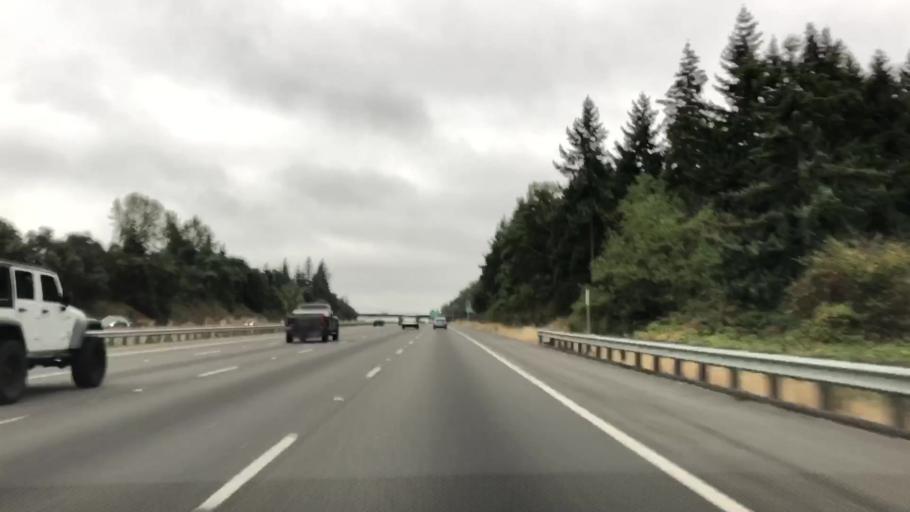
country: US
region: Washington
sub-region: King County
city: SeaTac
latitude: 47.4130
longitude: -122.2901
